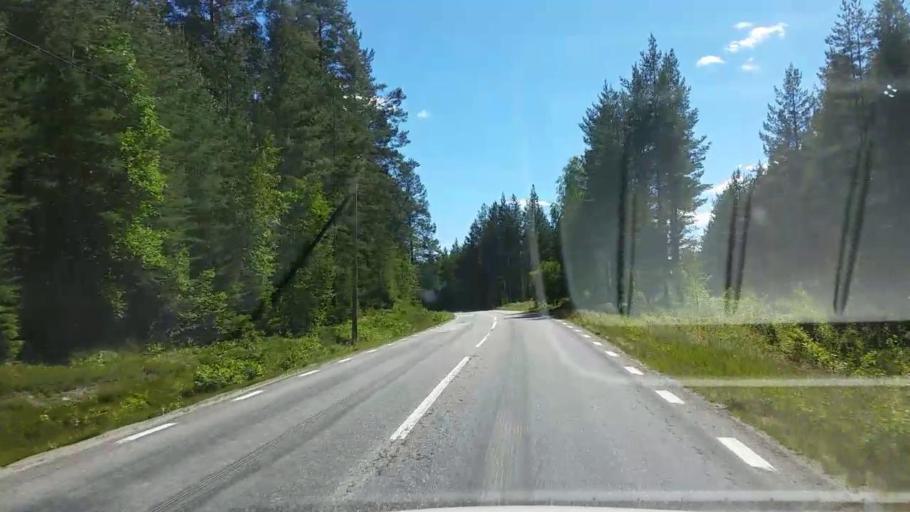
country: SE
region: Gaevleborg
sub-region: Ovanakers Kommun
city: Edsbyn
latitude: 61.2965
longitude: 15.8907
